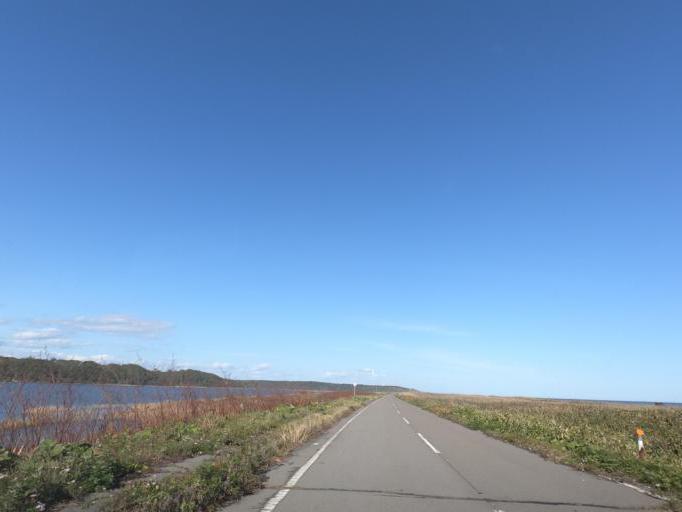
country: JP
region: Hokkaido
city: Obihiro
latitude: 42.5811
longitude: 143.5305
